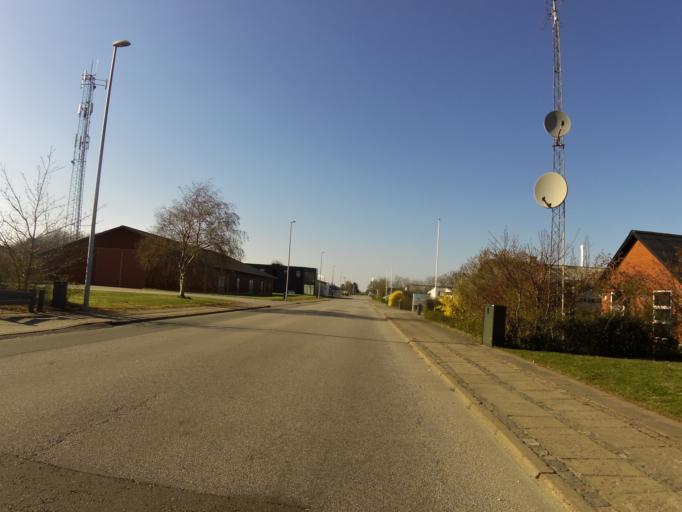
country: DK
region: South Denmark
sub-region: Esbjerg Kommune
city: Ribe
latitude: 55.3477
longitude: 8.7753
